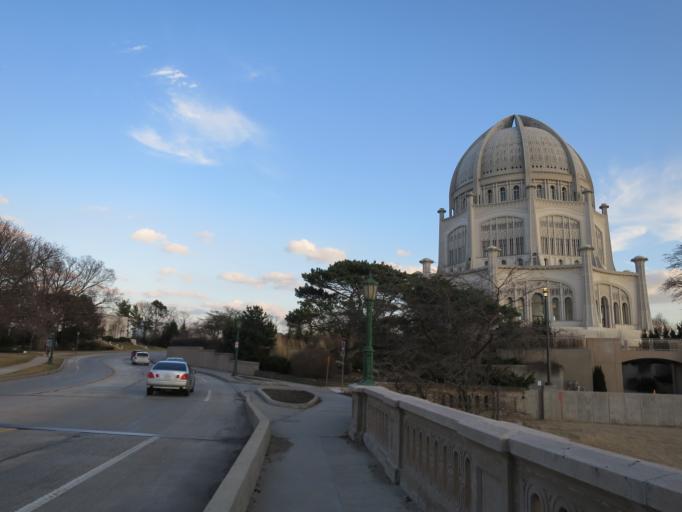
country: US
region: Illinois
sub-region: Cook County
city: Kenilworth
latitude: 42.0754
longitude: -87.6849
